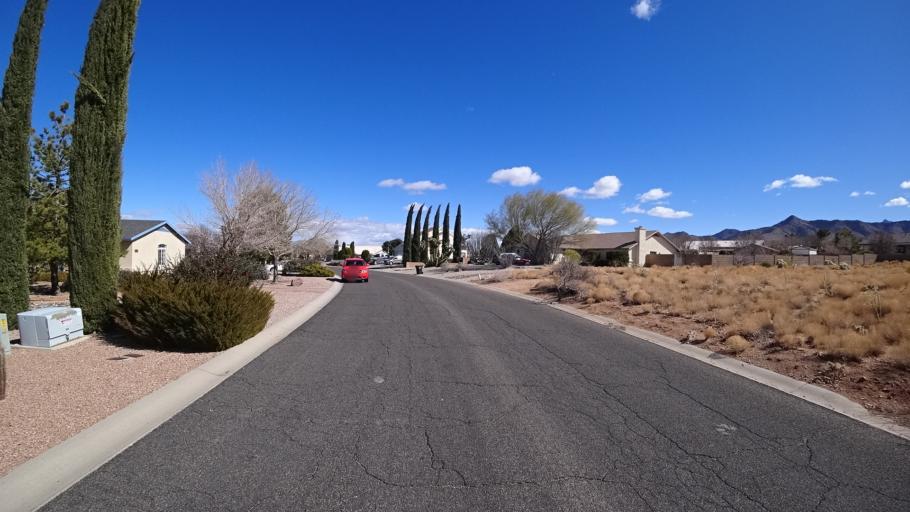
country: US
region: Arizona
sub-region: Mohave County
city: Kingman
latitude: 35.1988
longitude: -113.9732
